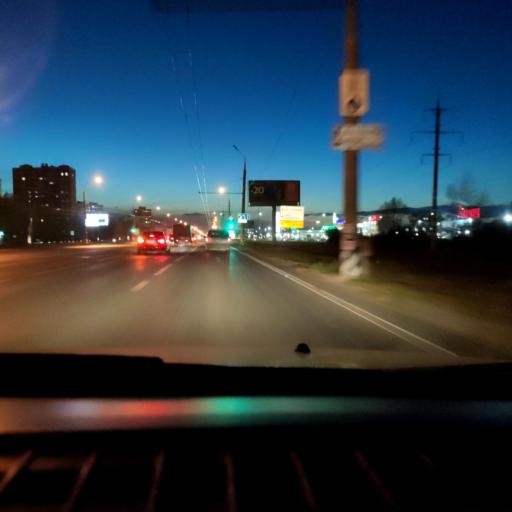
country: RU
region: Samara
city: Tol'yatti
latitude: 53.5484
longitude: 49.3494
